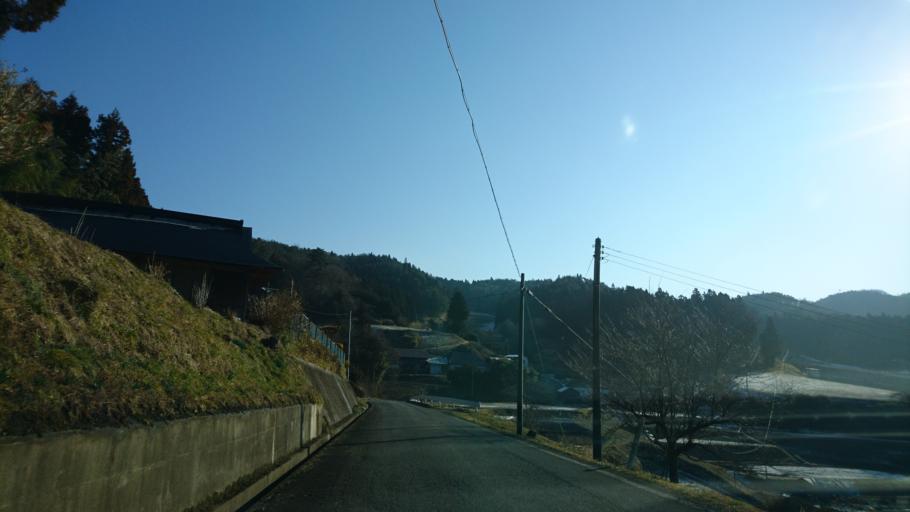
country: JP
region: Iwate
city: Ichinoseki
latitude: 38.9173
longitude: 141.2899
